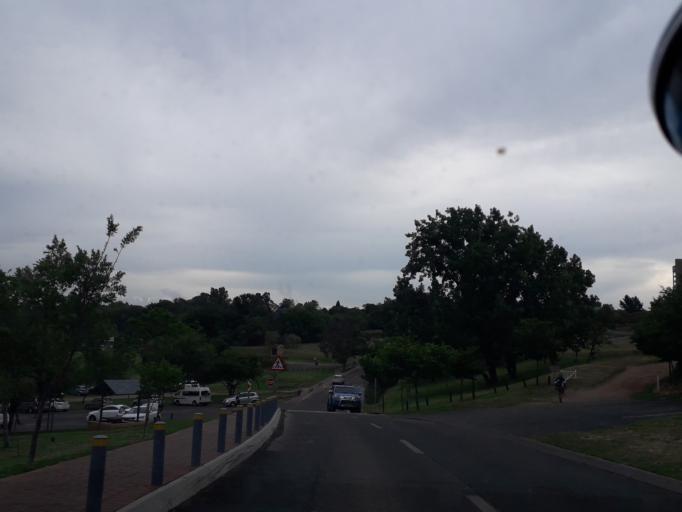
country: ZA
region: Gauteng
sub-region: City of Johannesburg Metropolitan Municipality
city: Johannesburg
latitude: -26.0827
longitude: 28.0134
